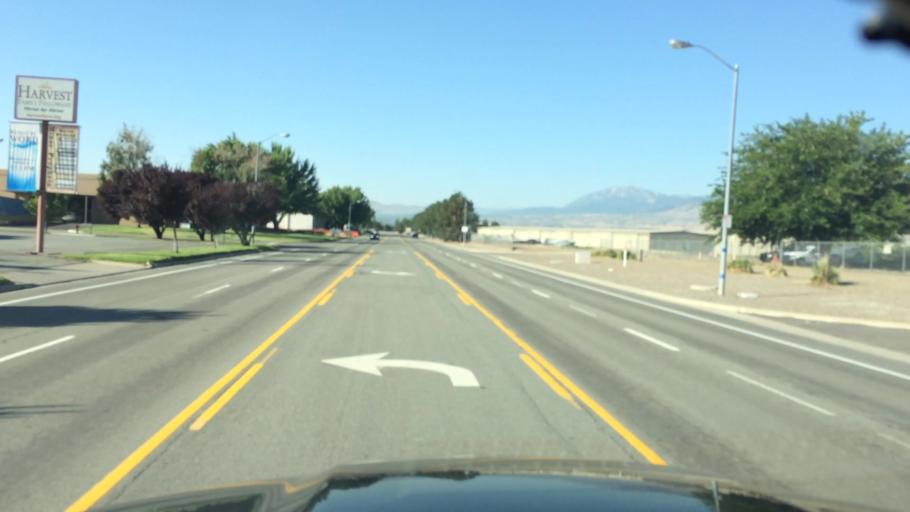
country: US
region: Nevada
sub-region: Washoe County
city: Sparks
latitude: 39.5099
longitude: -119.7631
